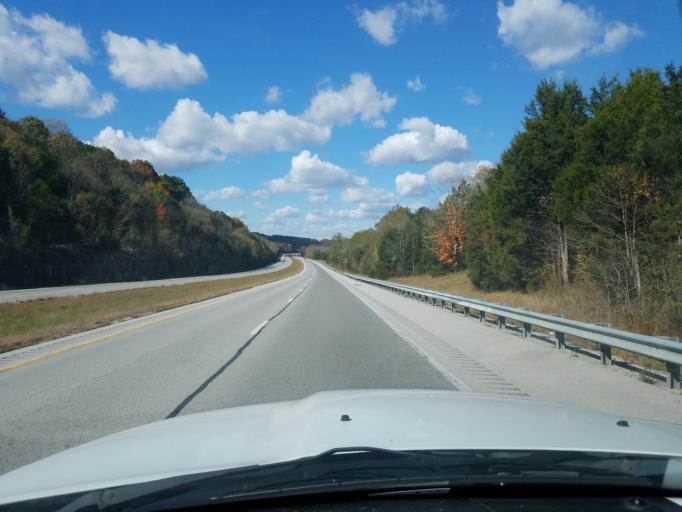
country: US
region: Kentucky
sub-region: Warren County
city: Bowling Green
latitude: 37.0398
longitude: -86.5622
